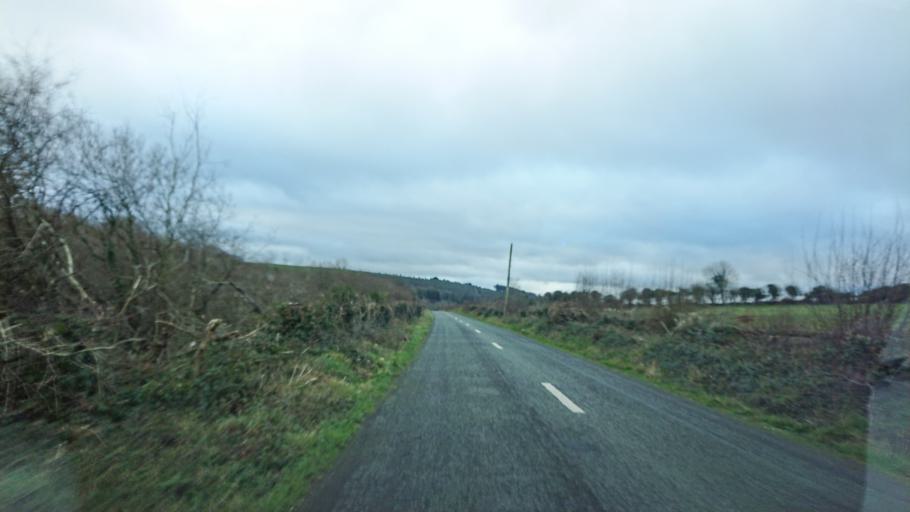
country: IE
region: Munster
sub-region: Waterford
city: Portlaw
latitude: 52.2337
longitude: -7.4111
